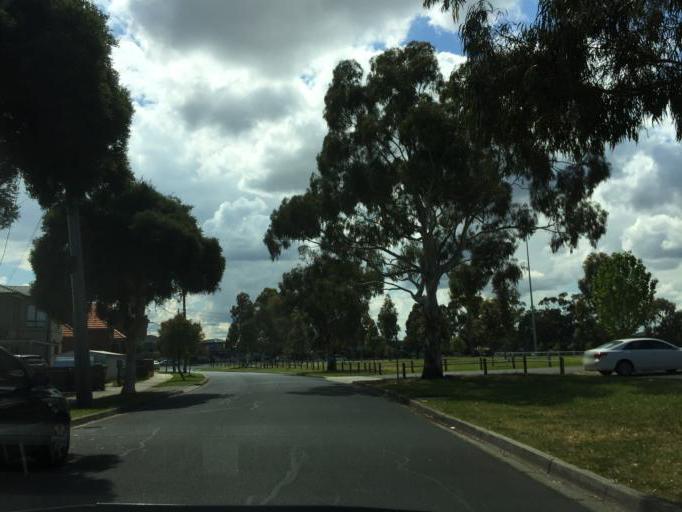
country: AU
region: Victoria
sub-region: Maribyrnong
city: Braybrook
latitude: -37.7886
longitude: 144.8654
